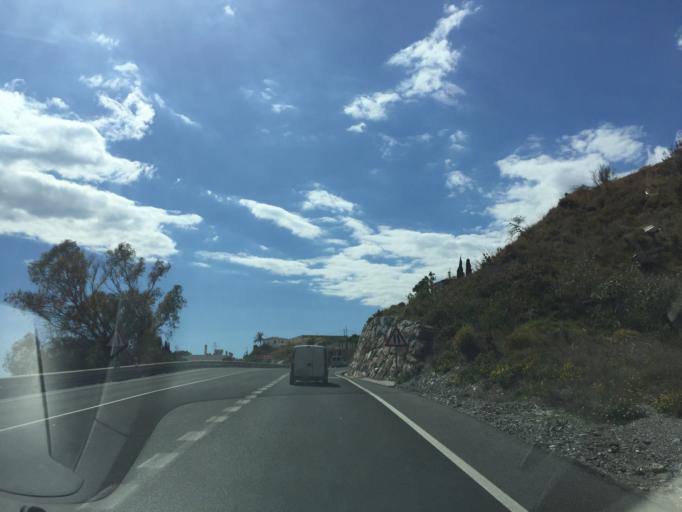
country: ES
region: Andalusia
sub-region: Provincia de Granada
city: Almunecar
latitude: 36.7393
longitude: -3.7069
